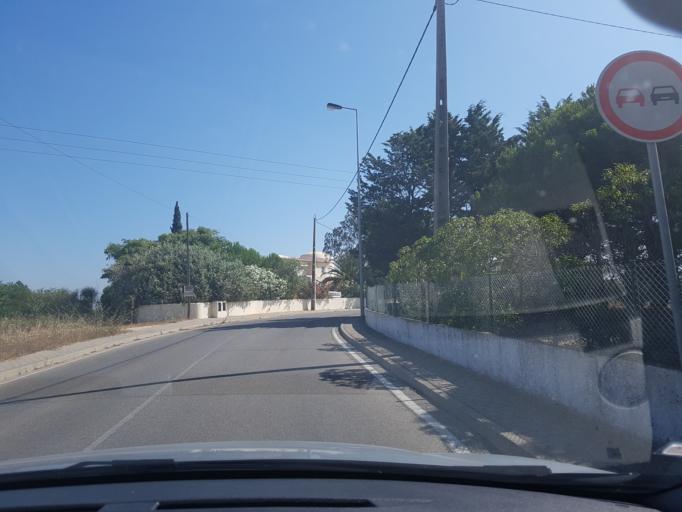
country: PT
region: Faro
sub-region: Lagoa
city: Carvoeiro
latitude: 37.1031
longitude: -8.4403
